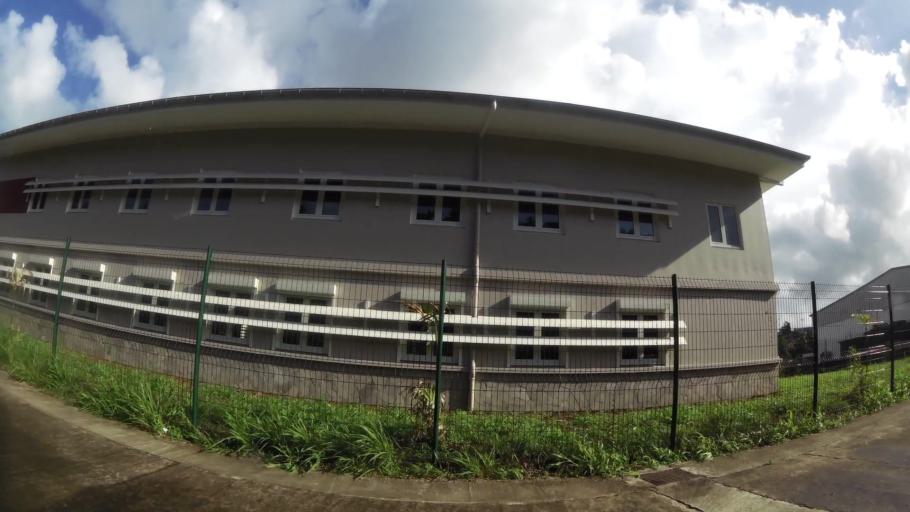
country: MQ
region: Martinique
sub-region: Martinique
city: Ducos
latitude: 14.5239
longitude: -60.9780
